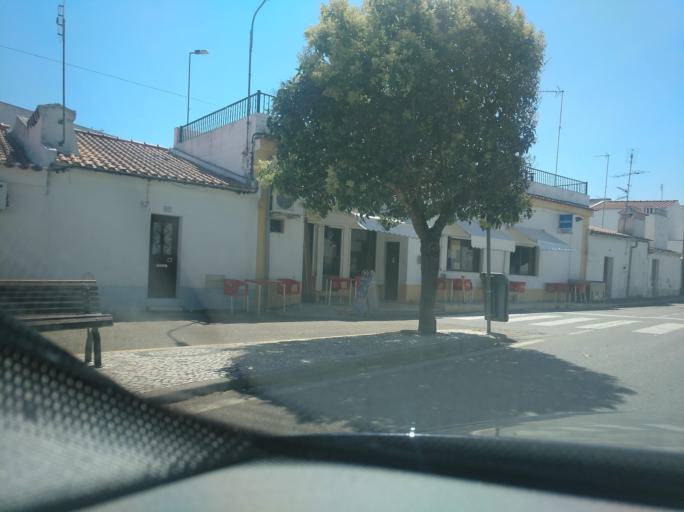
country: PT
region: Portalegre
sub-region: Elvas
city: Elvas
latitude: 38.9603
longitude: -7.2974
